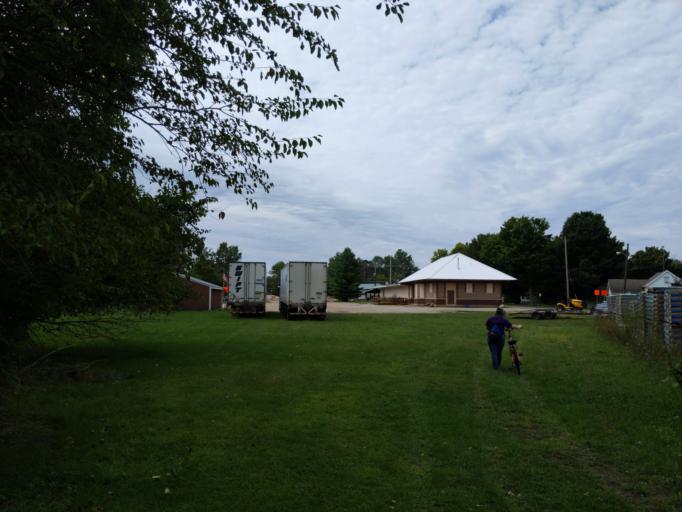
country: US
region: Michigan
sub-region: Barry County
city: Nashville
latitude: 42.6015
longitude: -85.0913
